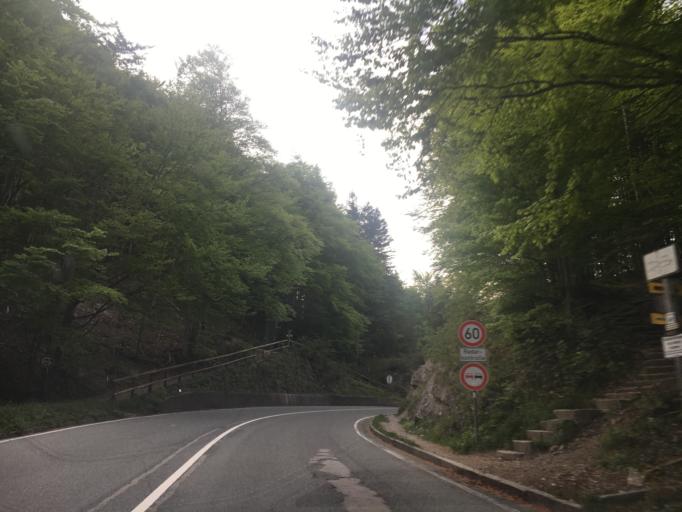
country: DE
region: Bavaria
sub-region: Upper Bavaria
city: Kochel
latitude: 47.6208
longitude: 11.3494
